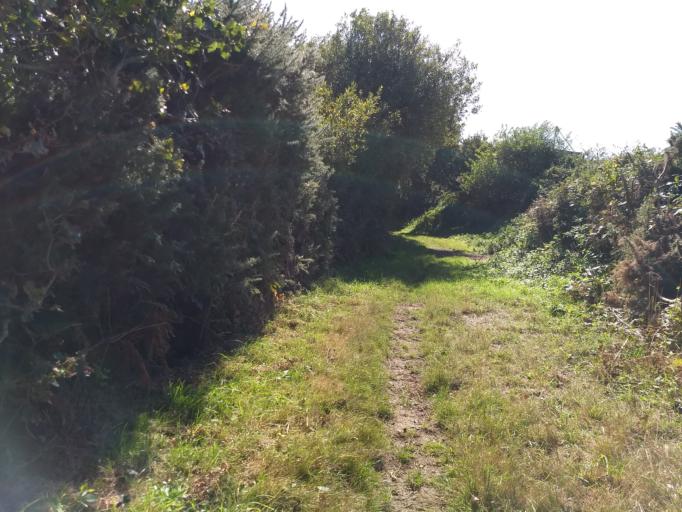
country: GB
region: England
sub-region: Isle of Wight
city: Niton
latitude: 50.6347
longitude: -1.2764
